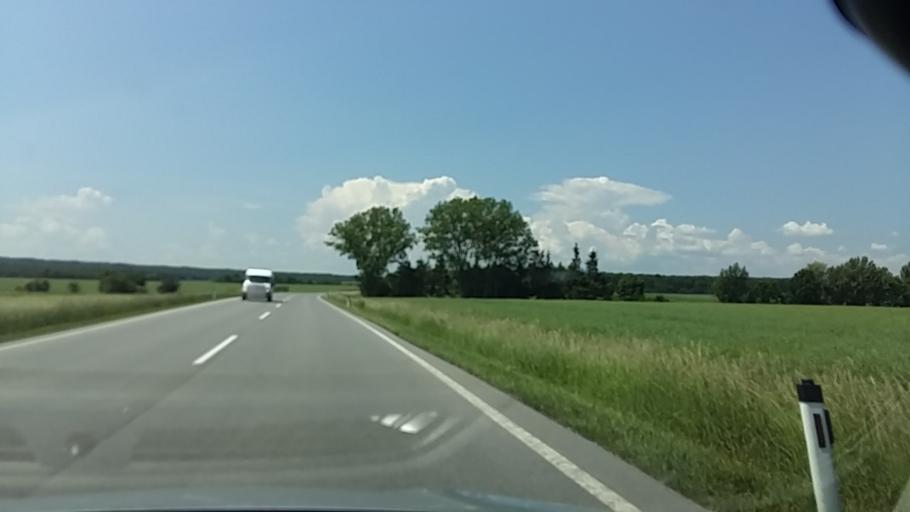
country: AT
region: Burgenland
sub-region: Politischer Bezirk Oberpullendorf
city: Raiding
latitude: 47.5348
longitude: 16.5403
